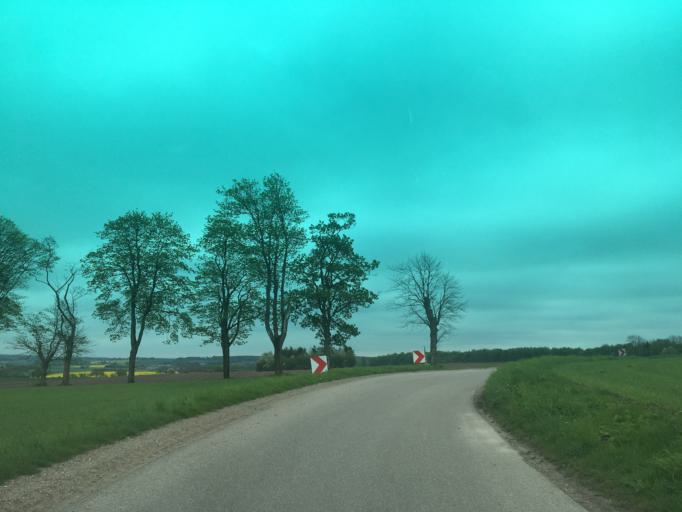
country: DK
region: Zealand
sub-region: Soro Kommune
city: Frederiksberg
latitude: 55.4031
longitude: 11.6570
